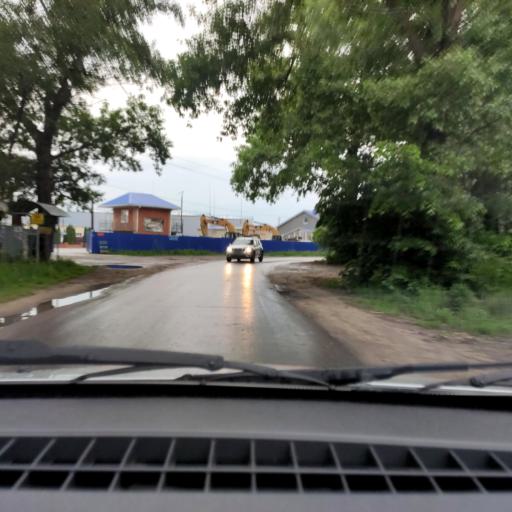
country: RU
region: Voronezj
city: Ramon'
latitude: 51.8471
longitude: 39.2260
